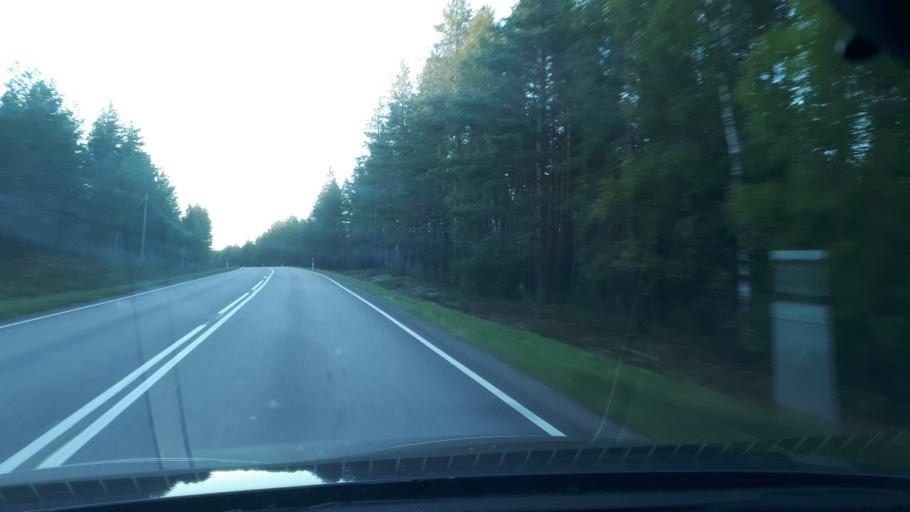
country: FI
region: Northern Ostrobothnia
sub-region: Haapavesi-Siikalatva
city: Pulkkila
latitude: 64.2559
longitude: 25.8785
